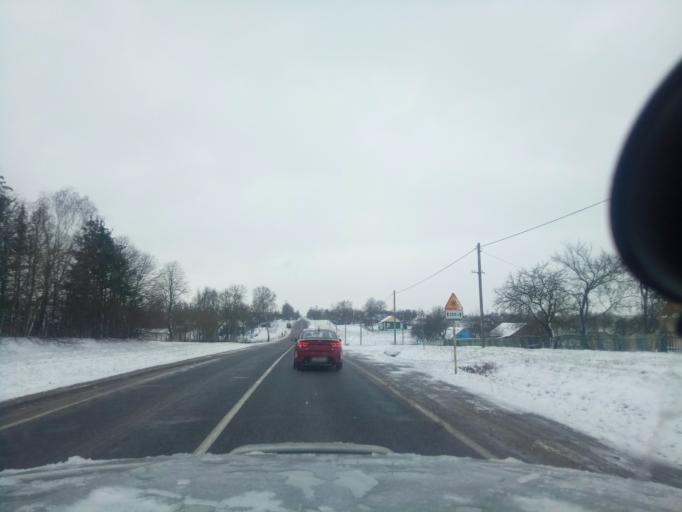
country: BY
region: Minsk
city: Klyetsk
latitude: 53.1327
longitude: 26.6732
